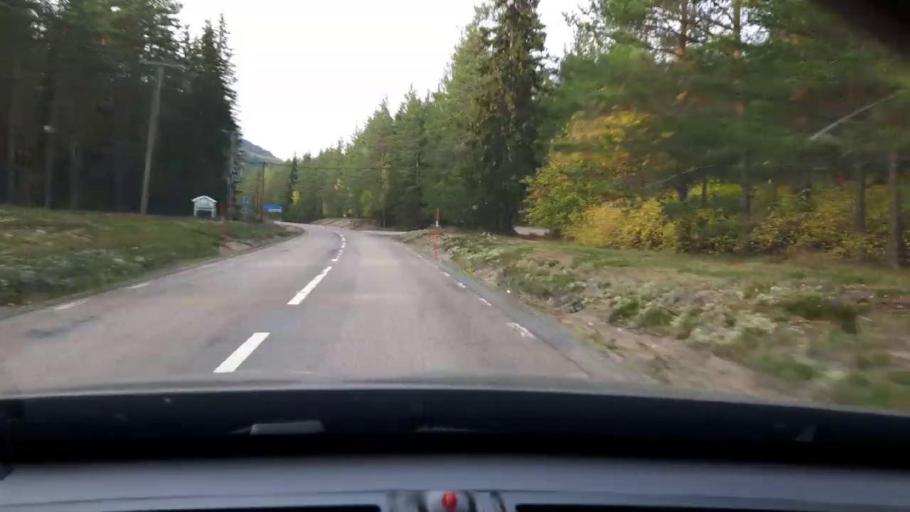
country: SE
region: Dalarna
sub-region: Gagnefs Kommun
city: Mockfjard
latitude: 60.2992
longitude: 14.9547
